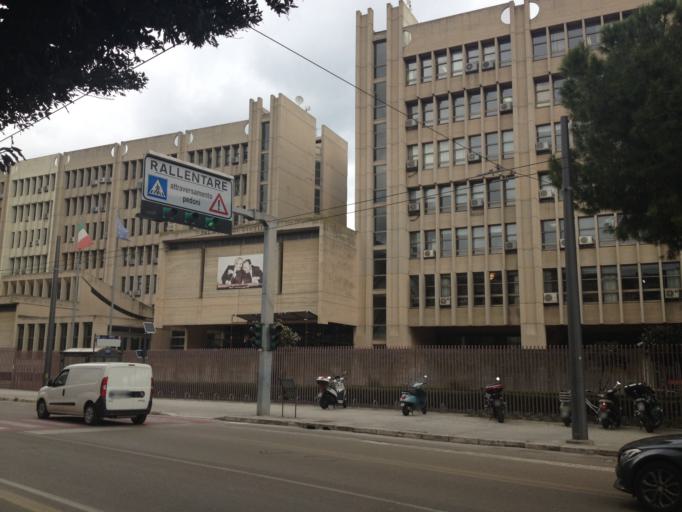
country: IT
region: Apulia
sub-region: Provincia di Lecce
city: Lecce
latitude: 40.3588
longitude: 18.1733
